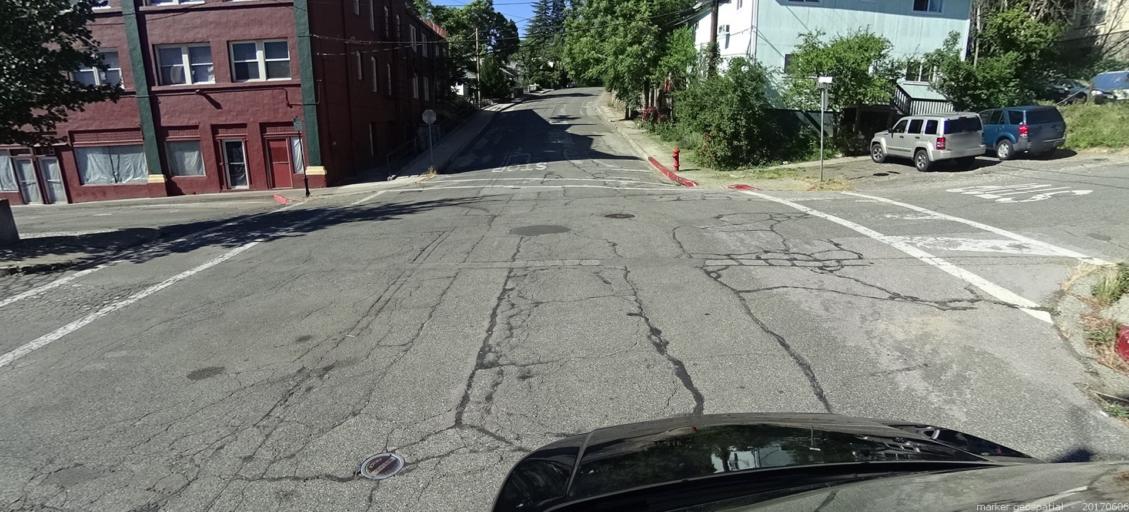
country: US
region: California
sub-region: Siskiyou County
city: Dunsmuir
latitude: 41.2113
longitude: -122.2726
